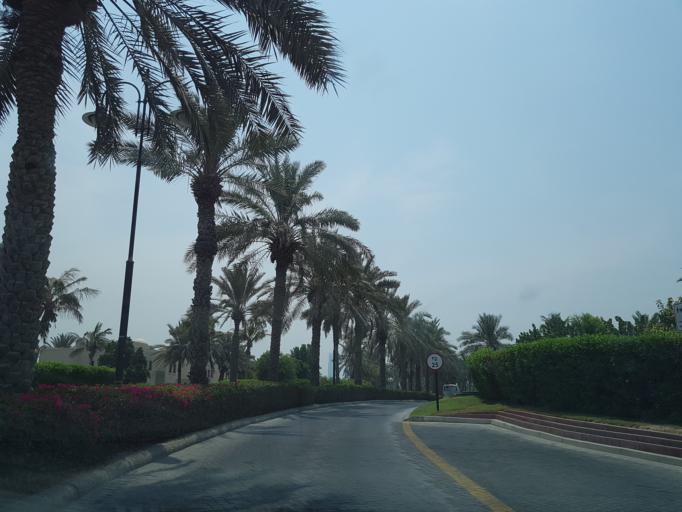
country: AE
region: Ash Shariqah
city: Sharjah
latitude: 25.2508
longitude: 55.3295
